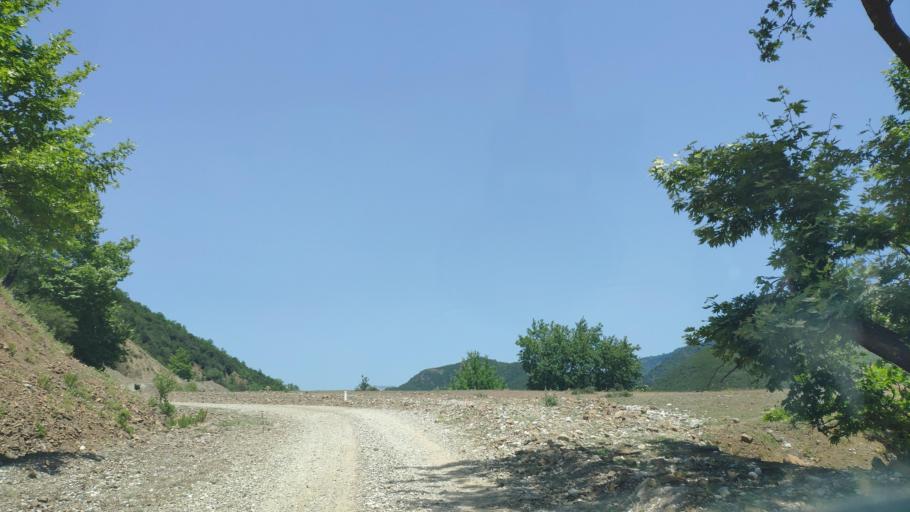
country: GR
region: Thessaly
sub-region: Nomos Kardhitsas
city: Anthiro
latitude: 39.1700
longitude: 21.3715
